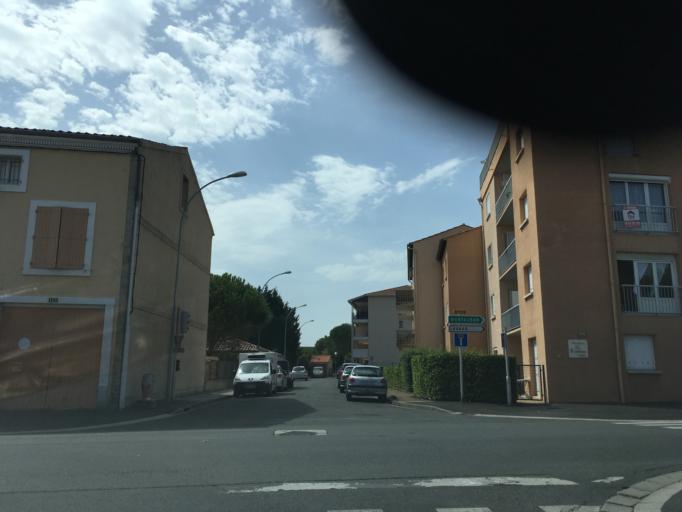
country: FR
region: Midi-Pyrenees
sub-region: Departement du Tarn
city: Castres
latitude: 43.6088
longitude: 2.2312
